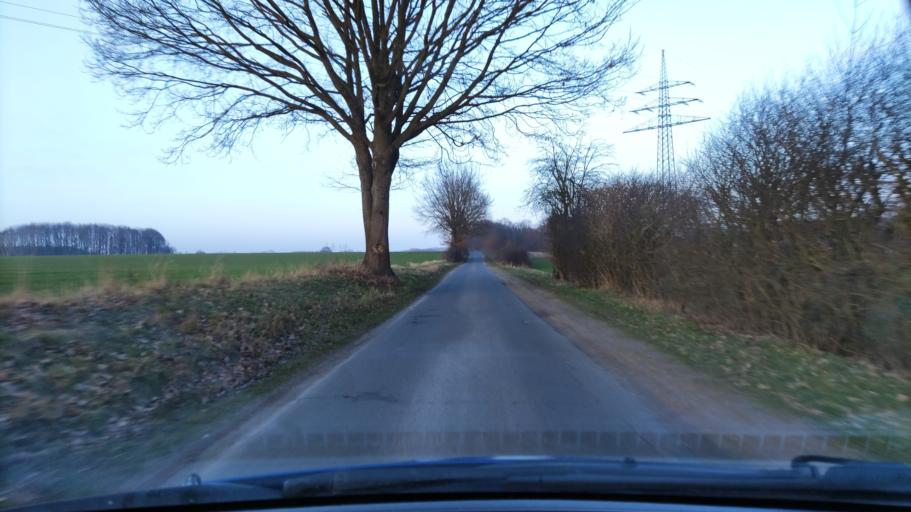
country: DE
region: Lower Saxony
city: Gerdau
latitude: 52.9952
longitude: 10.3930
